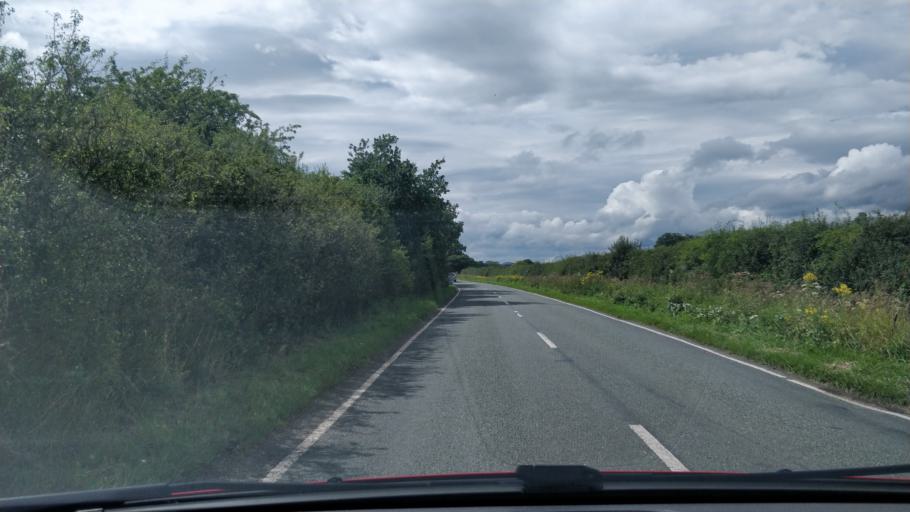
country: GB
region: Wales
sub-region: Wrexham
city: Rossett
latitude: 53.1534
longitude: -2.9448
